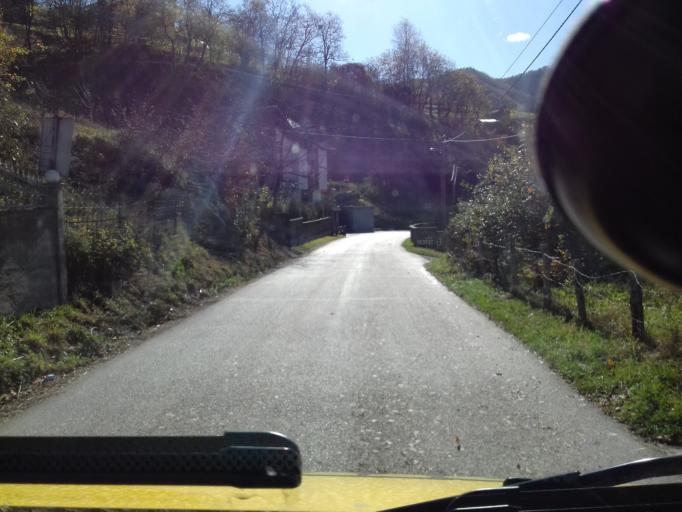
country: BA
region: Federation of Bosnia and Herzegovina
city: Zenica
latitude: 44.1809
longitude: 17.9040
